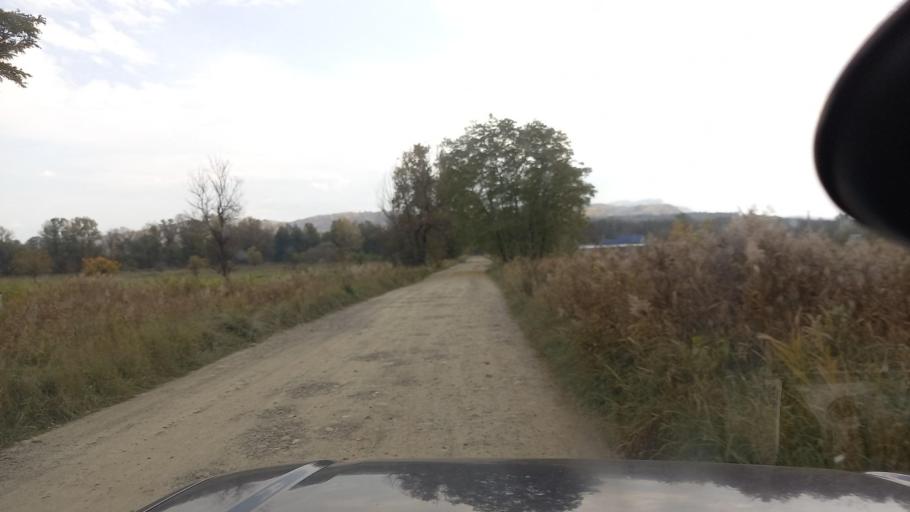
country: RU
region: Krasnodarskiy
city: Shedok
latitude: 44.1833
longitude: 40.8442
